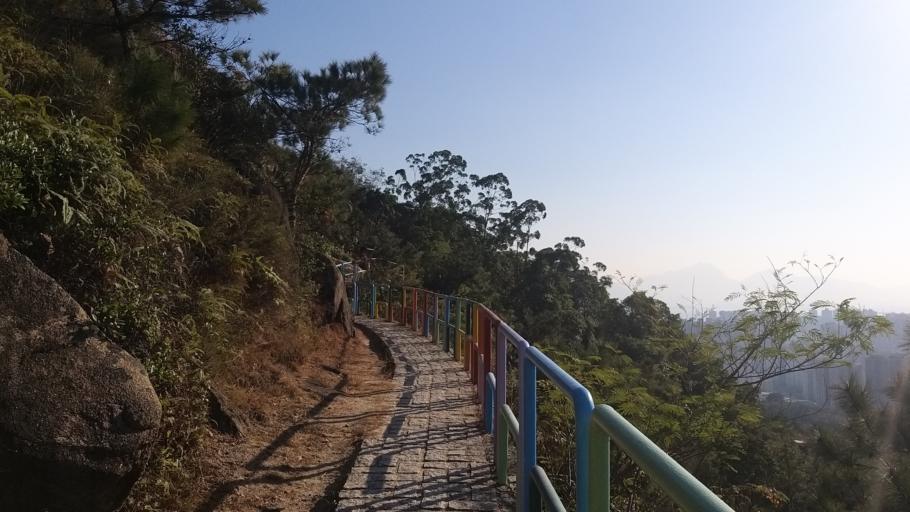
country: HK
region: Tuen Mun
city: Tuen Mun
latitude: 22.3989
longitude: 113.9835
